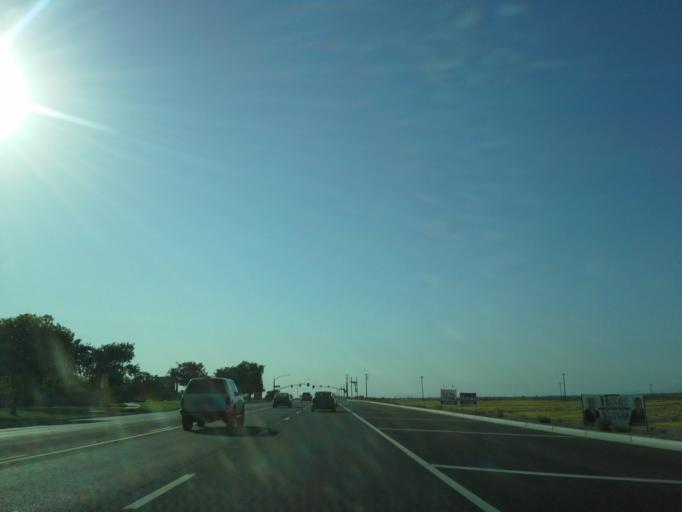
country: US
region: Arizona
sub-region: Pinal County
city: San Tan Valley
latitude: 33.1889
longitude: -111.5973
